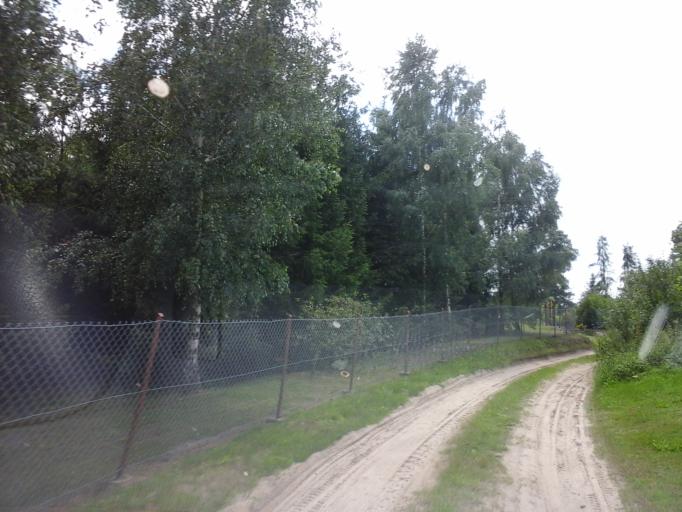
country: PL
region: Lubusz
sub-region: Powiat strzelecko-drezdenecki
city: Dobiegniew
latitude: 53.0534
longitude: 15.7499
